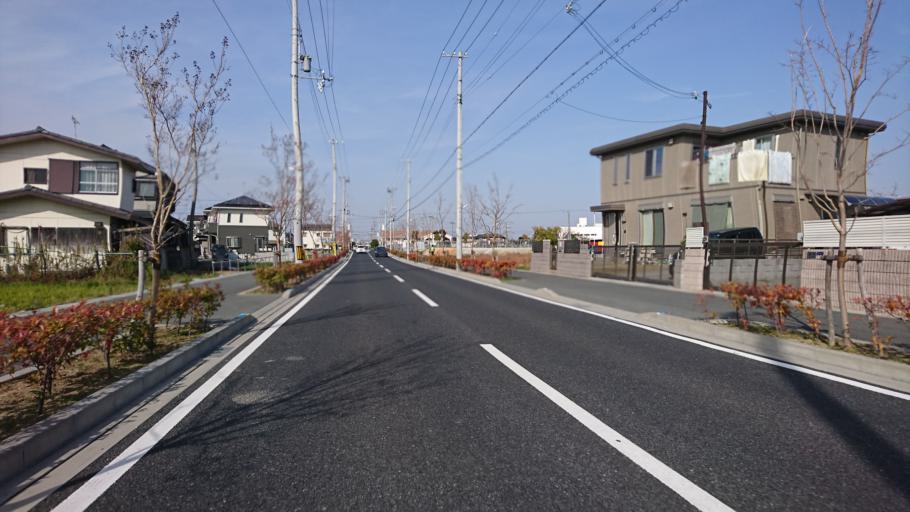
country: JP
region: Hyogo
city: Kakogawacho-honmachi
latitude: 34.7125
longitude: 134.8683
